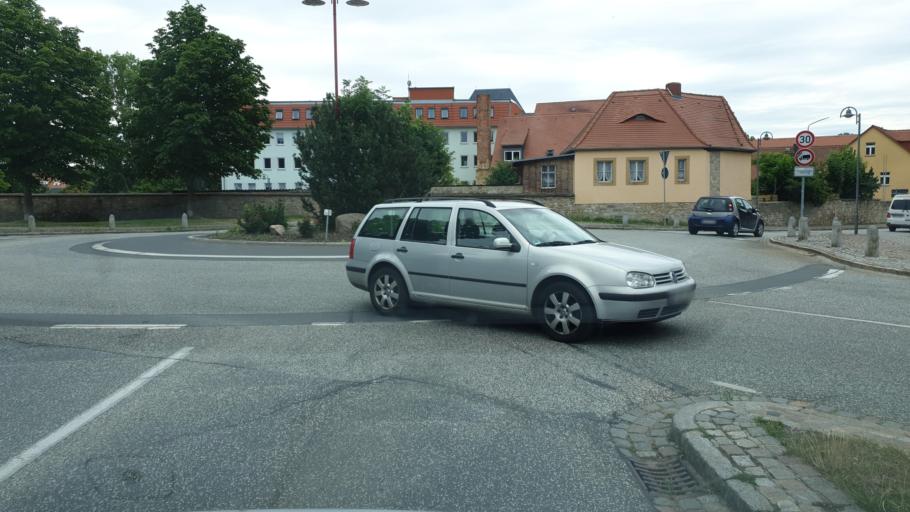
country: DE
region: Saxony-Anhalt
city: Querfurt
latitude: 51.3829
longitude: 11.5997
